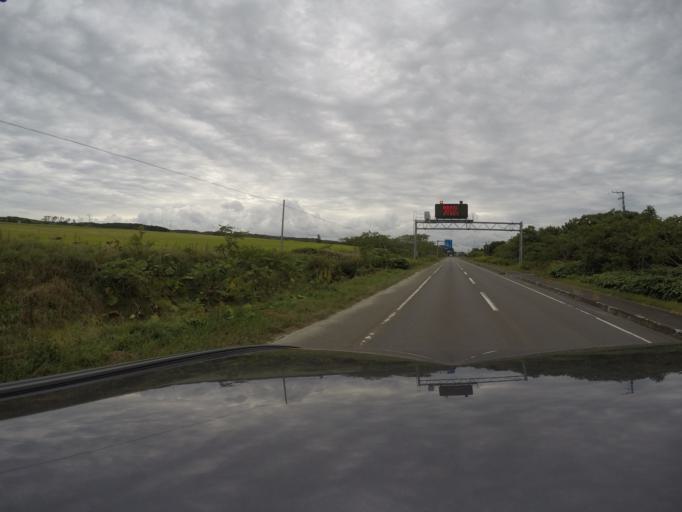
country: JP
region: Hokkaido
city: Makubetsu
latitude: 45.1507
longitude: 141.7511
